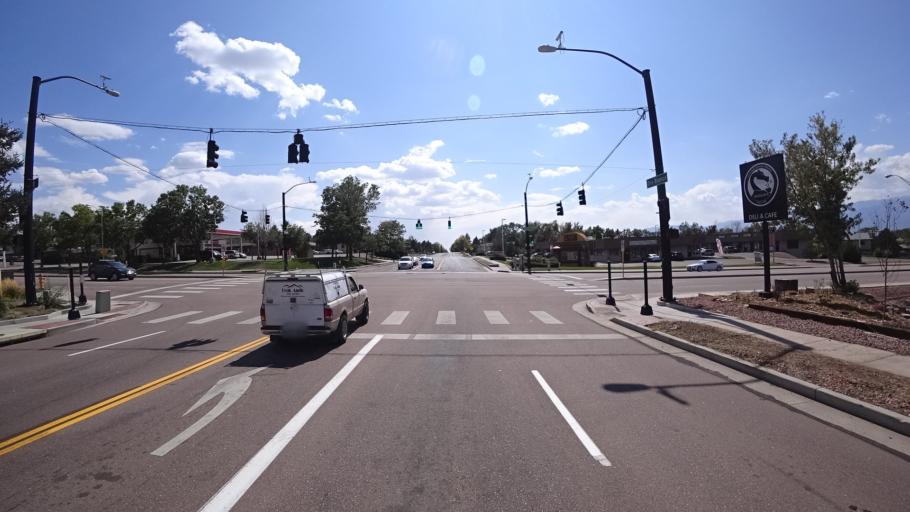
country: US
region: Colorado
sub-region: El Paso County
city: Cimarron Hills
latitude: 38.8972
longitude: -104.7385
